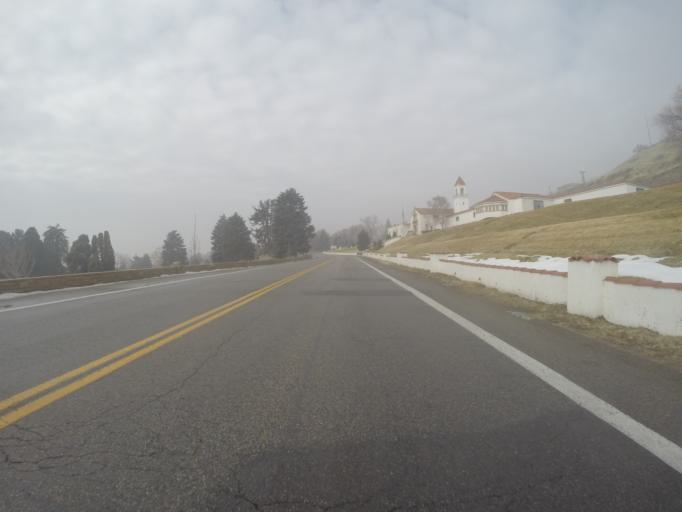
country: US
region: Utah
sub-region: Salt Lake County
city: Salt Lake City
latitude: 40.7800
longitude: -111.8588
